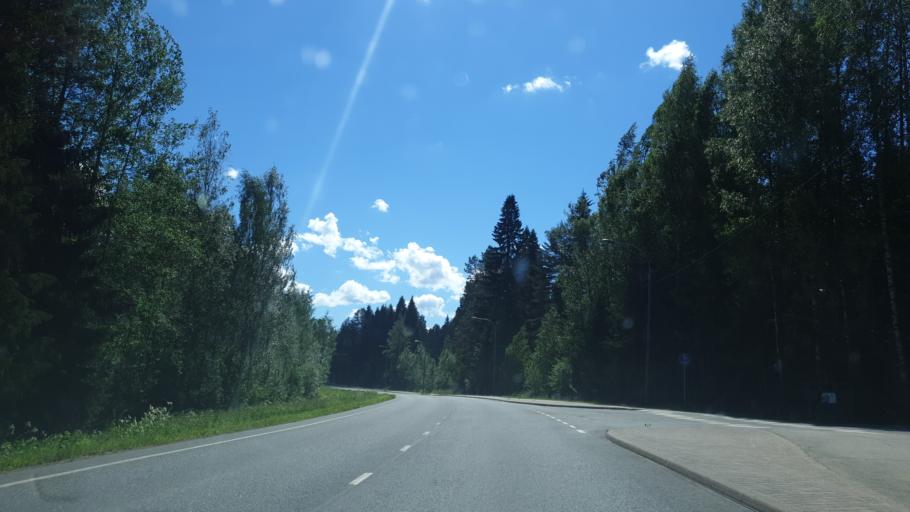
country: FI
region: Northern Savo
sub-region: Koillis-Savo
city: Kaavi
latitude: 62.9784
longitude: 28.4944
